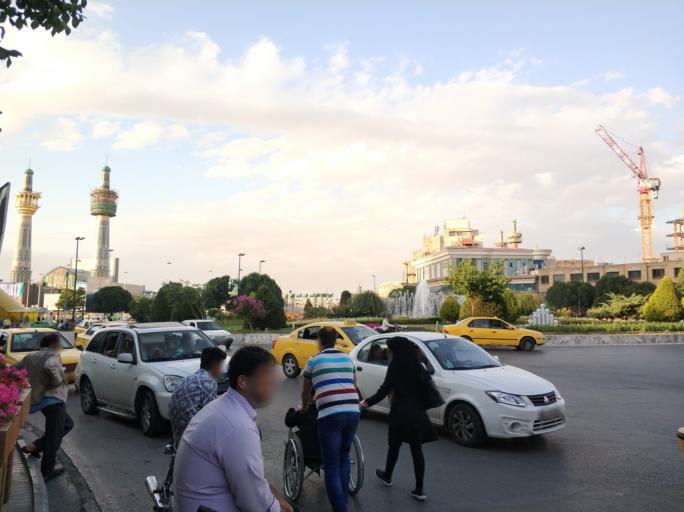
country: IR
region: Razavi Khorasan
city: Mashhad
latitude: 36.2835
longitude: 59.6117
